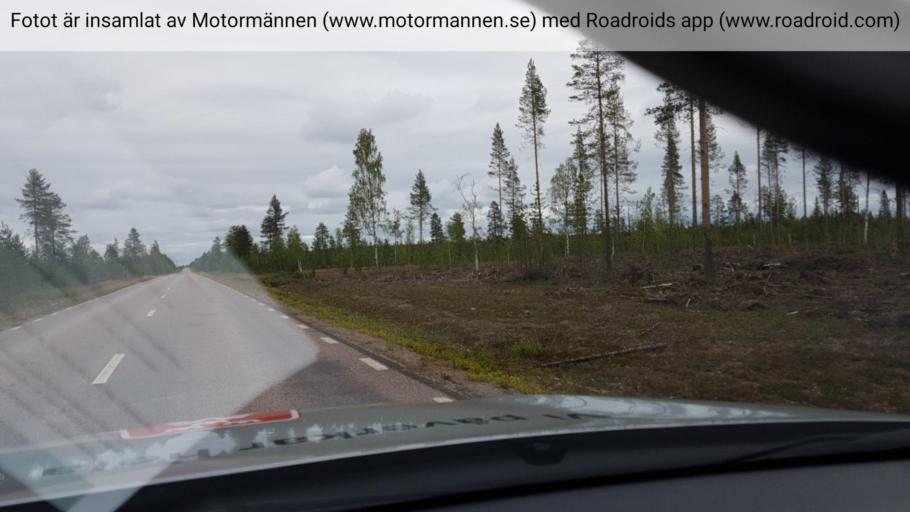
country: SE
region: Norrbotten
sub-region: Overkalix Kommun
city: OEverkalix
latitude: 67.0869
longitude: 22.5552
